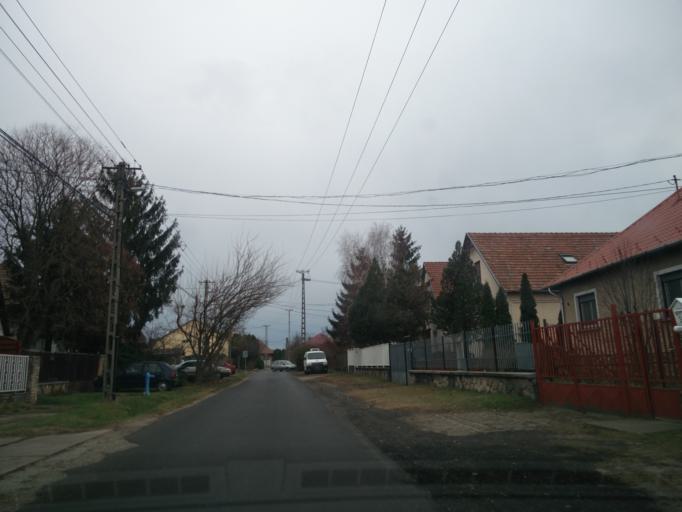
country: HU
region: Pest
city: Fot
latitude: 47.6569
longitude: 19.2316
